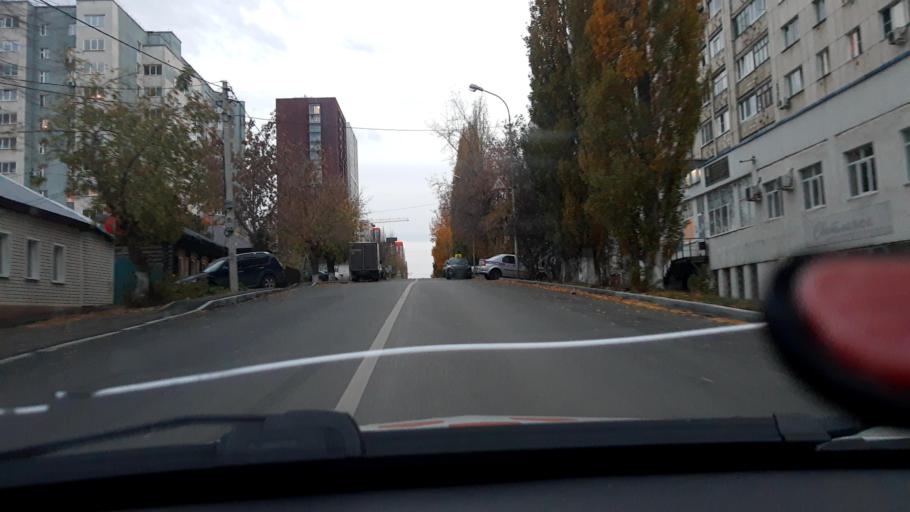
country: RU
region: Bashkortostan
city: Ufa
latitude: 54.7378
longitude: 55.9340
